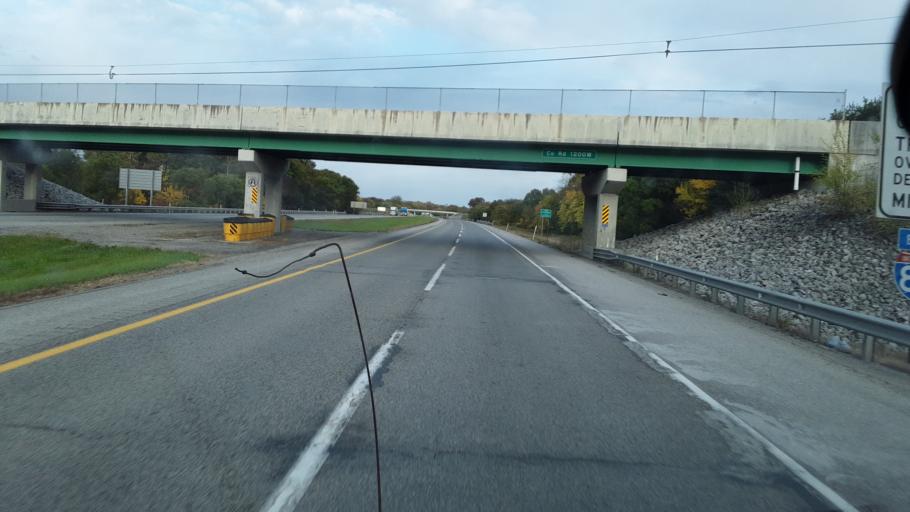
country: US
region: Michigan
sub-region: Saint Joseph County
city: White Pigeon
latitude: 41.7500
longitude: -85.6602
